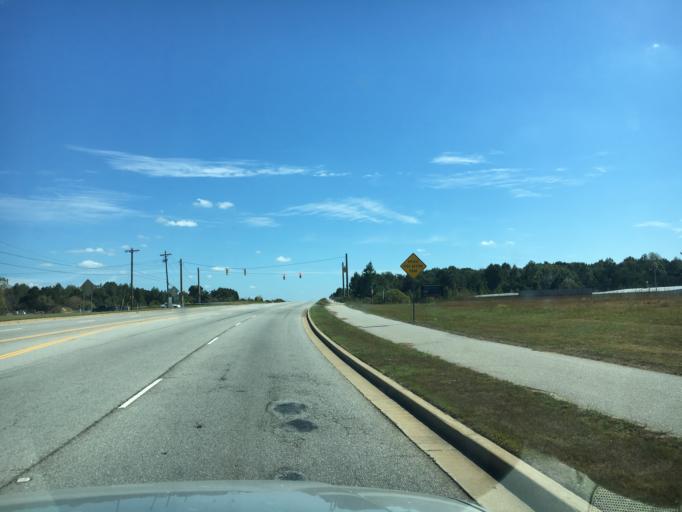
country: US
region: South Carolina
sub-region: Spartanburg County
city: Spartanburg
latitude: 34.9081
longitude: -81.9341
